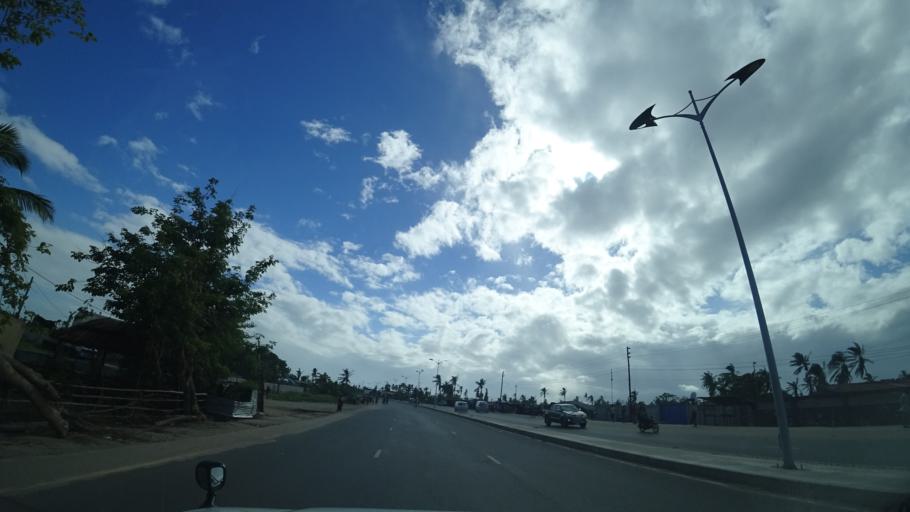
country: MZ
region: Sofala
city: Beira
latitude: -19.7775
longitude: 34.8821
